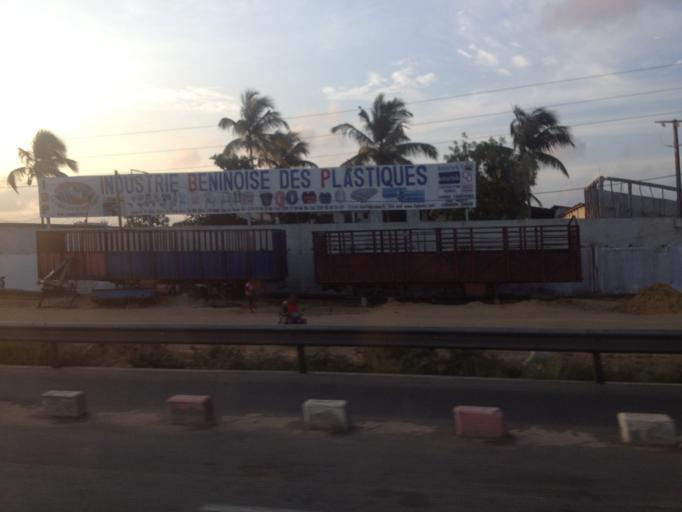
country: BJ
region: Littoral
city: Cotonou
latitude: 6.3726
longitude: 2.5411
